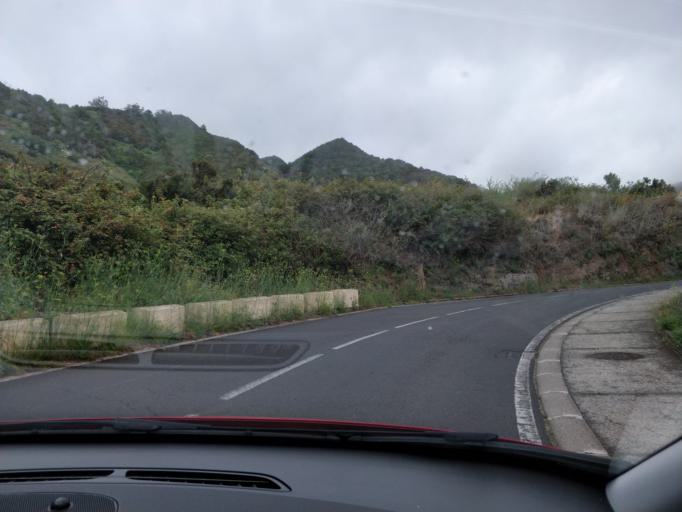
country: ES
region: Canary Islands
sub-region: Provincia de Santa Cruz de Tenerife
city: Tanque
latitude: 28.3286
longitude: -16.8432
